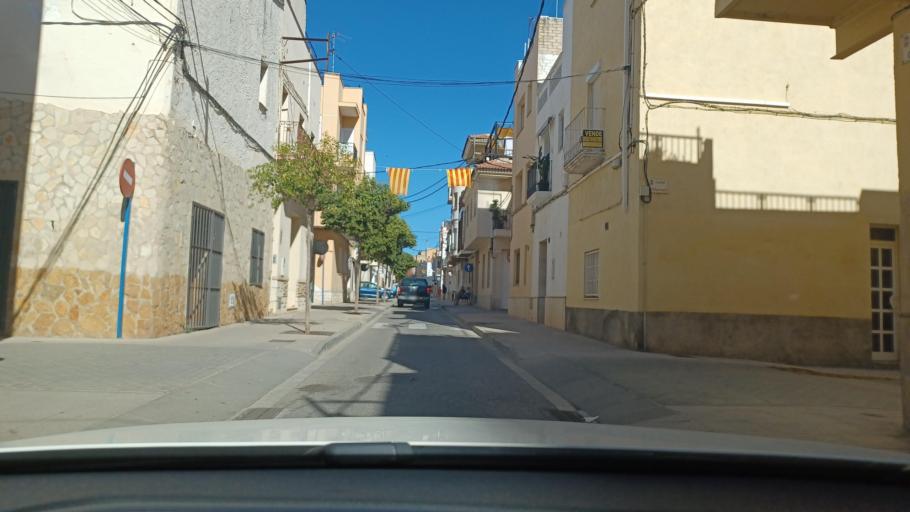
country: ES
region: Catalonia
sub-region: Provincia de Tarragona
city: Amposta
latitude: 40.7143
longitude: 0.5774
